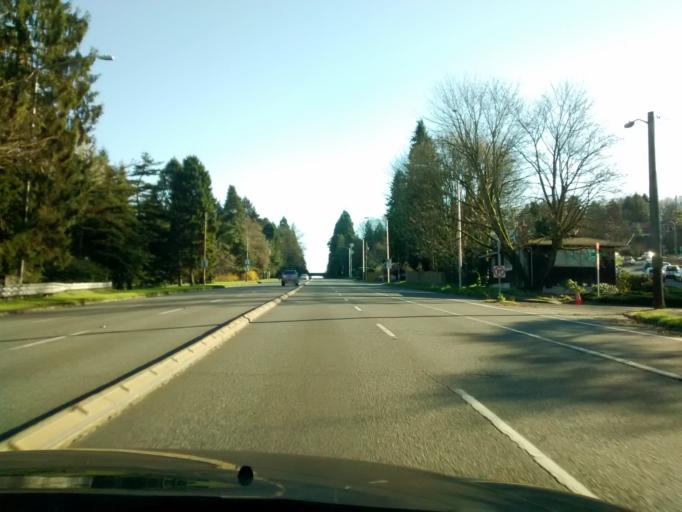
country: US
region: Washington
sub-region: King County
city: Seattle
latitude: 47.6741
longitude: -122.3472
